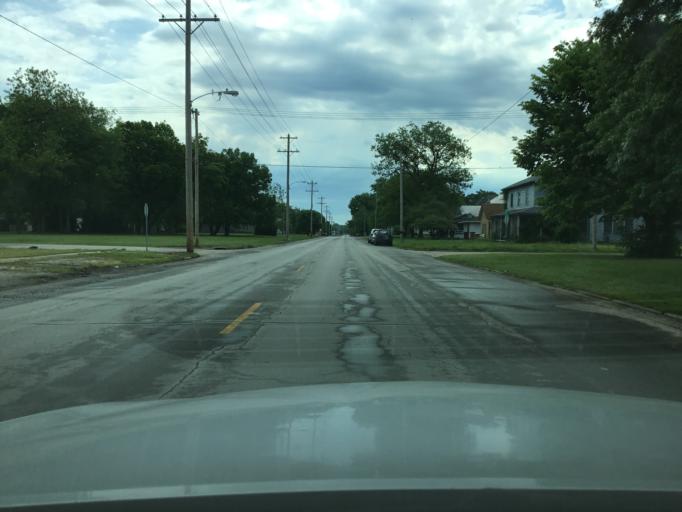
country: US
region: Kansas
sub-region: Montgomery County
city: Coffeyville
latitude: 37.0361
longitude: -95.6112
